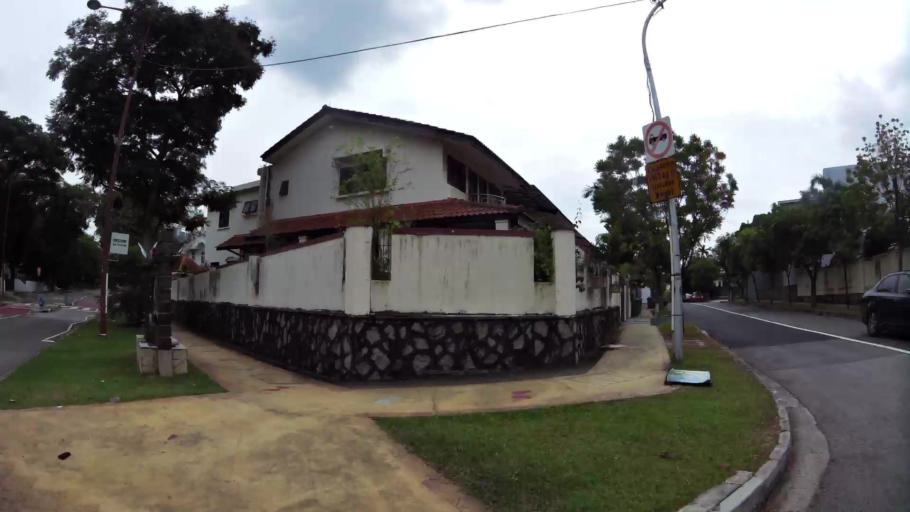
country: SG
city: Singapore
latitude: 1.3137
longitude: 103.7853
